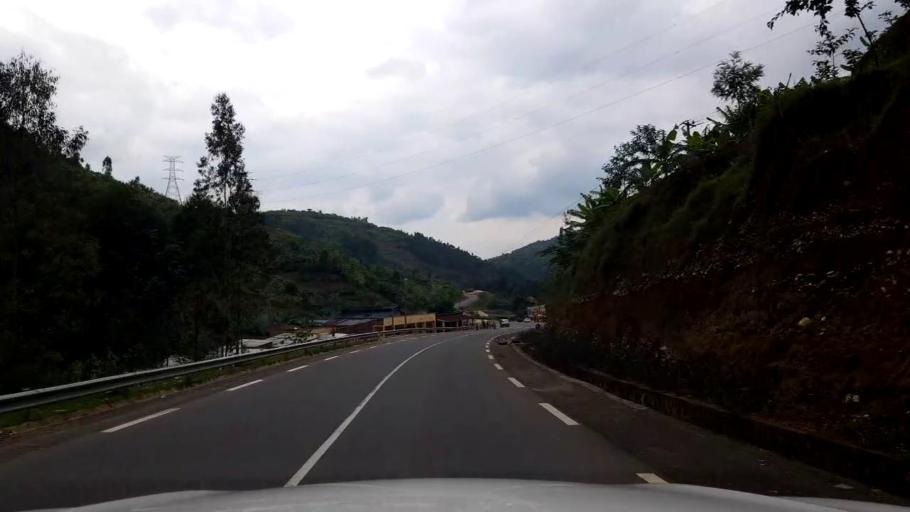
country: RW
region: Western Province
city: Kibuye
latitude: -1.9135
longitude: 29.3690
